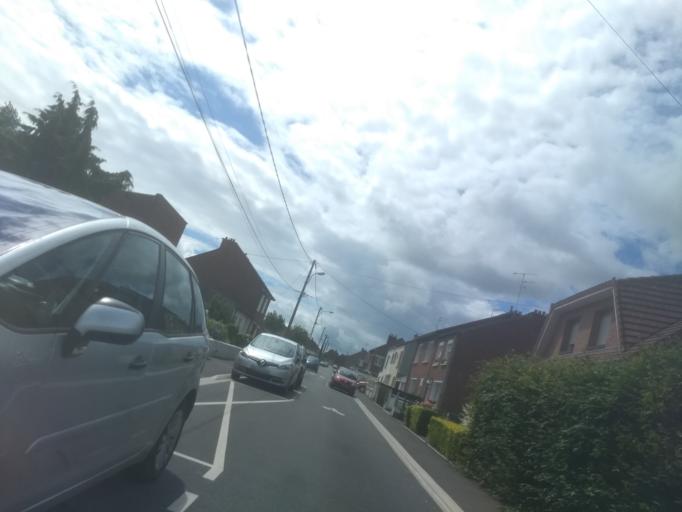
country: FR
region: Nord-Pas-de-Calais
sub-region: Departement du Pas-de-Calais
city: Agny
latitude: 50.2655
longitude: 2.7635
